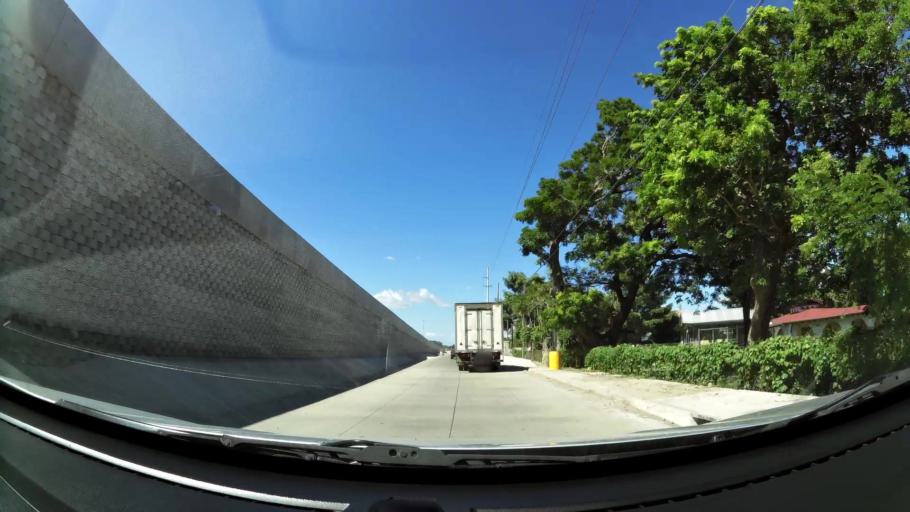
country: CR
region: Guanacaste
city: Liberia
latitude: 10.6129
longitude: -85.4345
